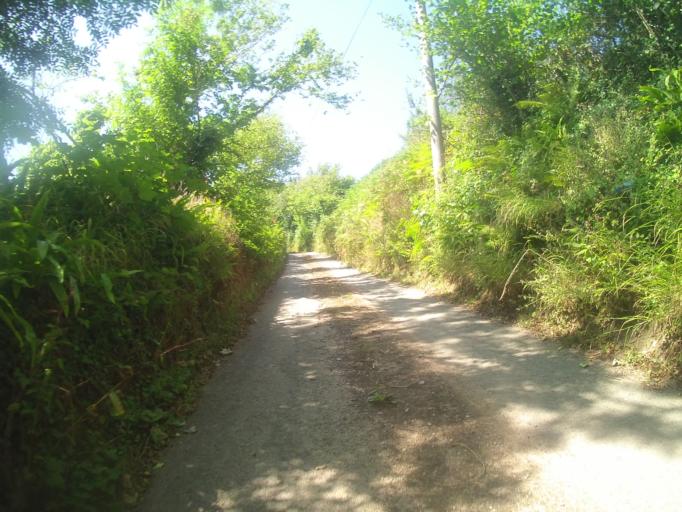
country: GB
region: England
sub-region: Devon
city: Dartmouth
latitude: 50.3588
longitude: -3.6163
